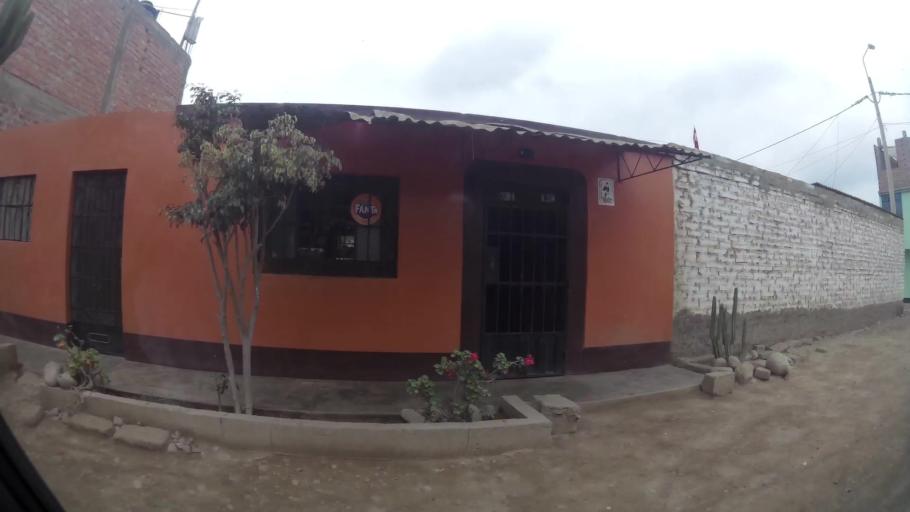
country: PE
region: Lima
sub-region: Provincia de Huaral
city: Huaral
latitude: -11.5012
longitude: -77.2319
